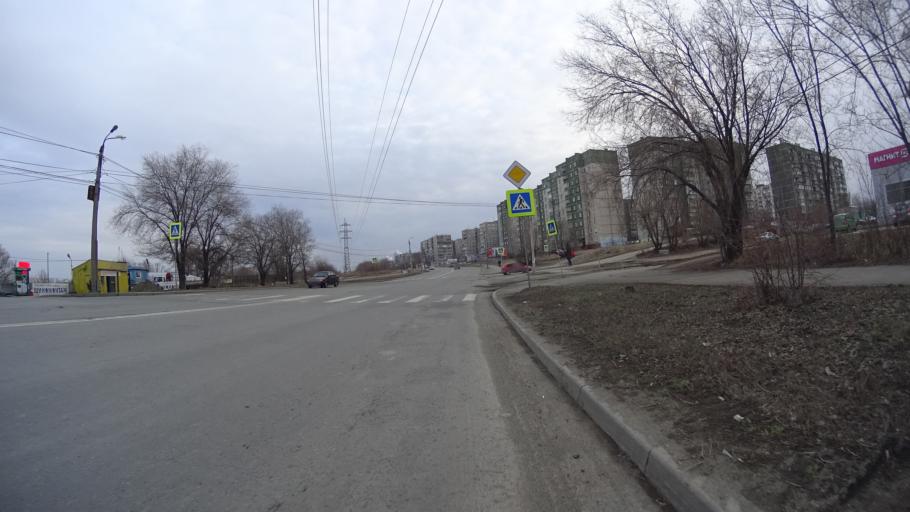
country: RU
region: Chelyabinsk
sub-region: Gorod Chelyabinsk
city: Chelyabinsk
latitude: 55.1871
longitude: 61.4844
